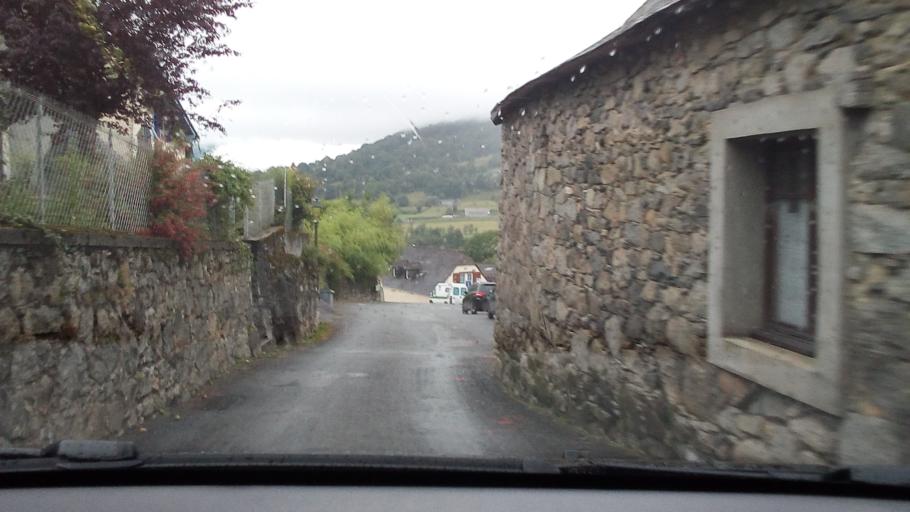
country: FR
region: Midi-Pyrenees
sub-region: Departement des Hautes-Pyrenees
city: Argeles-Gazost
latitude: 42.9913
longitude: -0.1257
